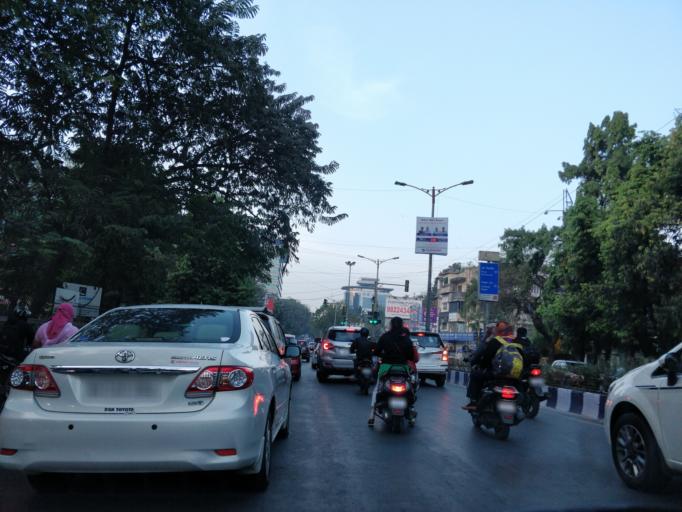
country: IN
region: Maharashtra
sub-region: Pune Division
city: Shivaji Nagar
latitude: 18.5284
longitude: 73.8299
